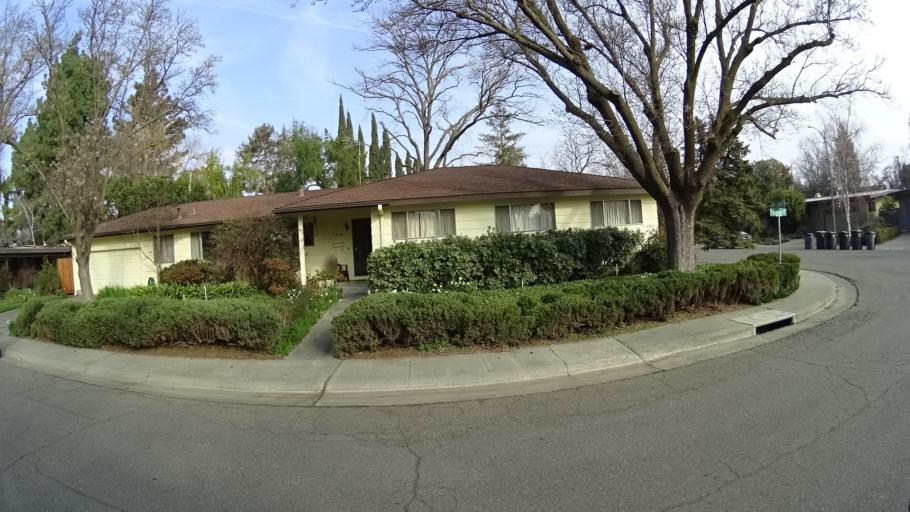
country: US
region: California
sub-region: Yolo County
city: Davis
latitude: 38.5570
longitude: -121.7617
